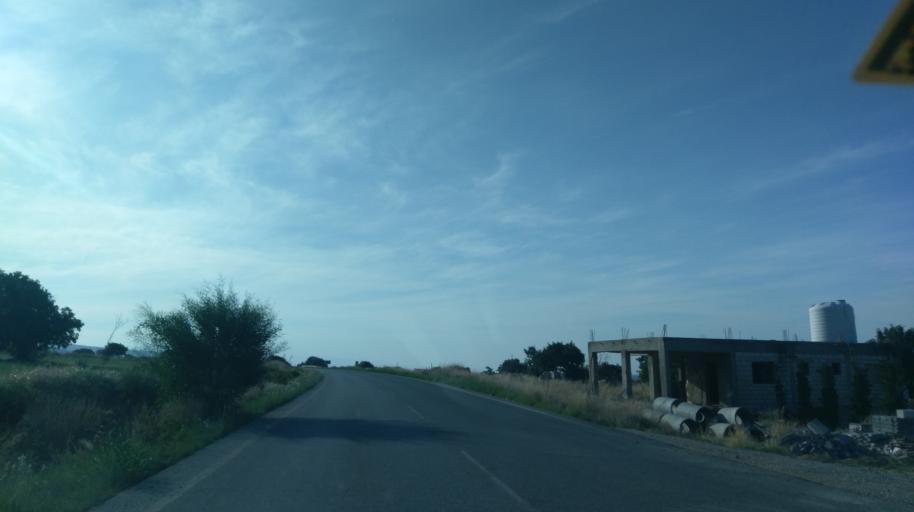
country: CY
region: Ammochostos
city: Lefkonoiko
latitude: 35.3627
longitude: 33.6740
